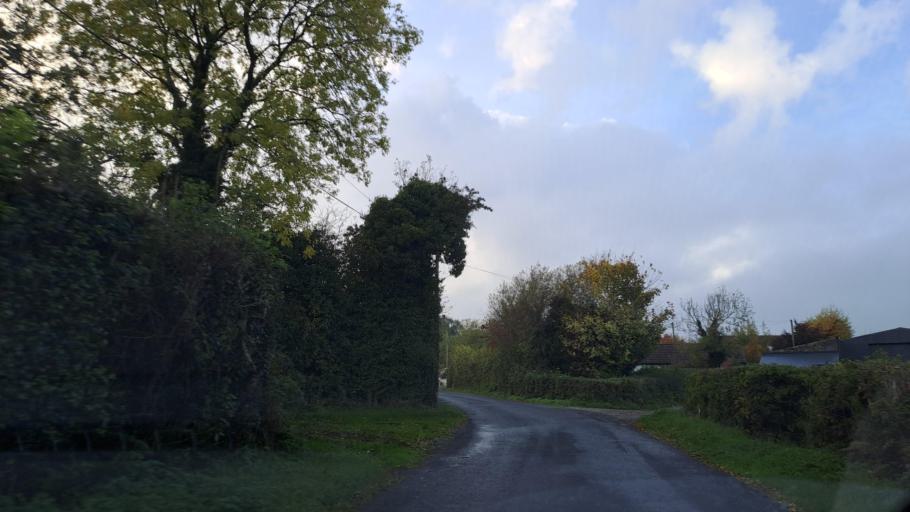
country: IE
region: Ulster
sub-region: County Monaghan
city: Carrickmacross
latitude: 53.9725
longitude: -6.7712
